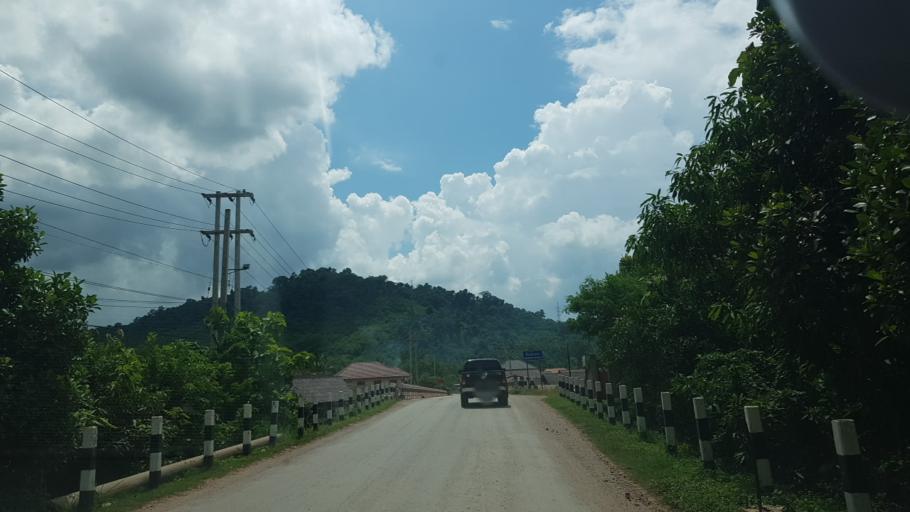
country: LA
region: Oudomxai
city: Muang Xay
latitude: 20.6625
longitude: 101.9757
